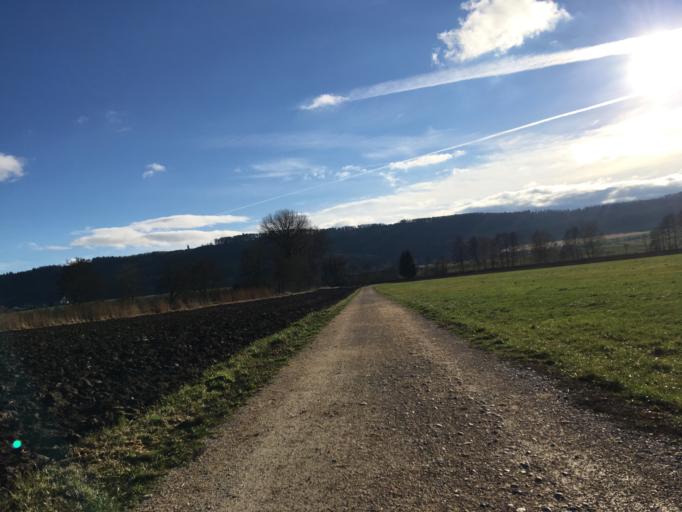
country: DE
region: Baden-Wuerttemberg
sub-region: Freiburg Region
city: Gottmadingen
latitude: 47.7252
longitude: 8.7704
